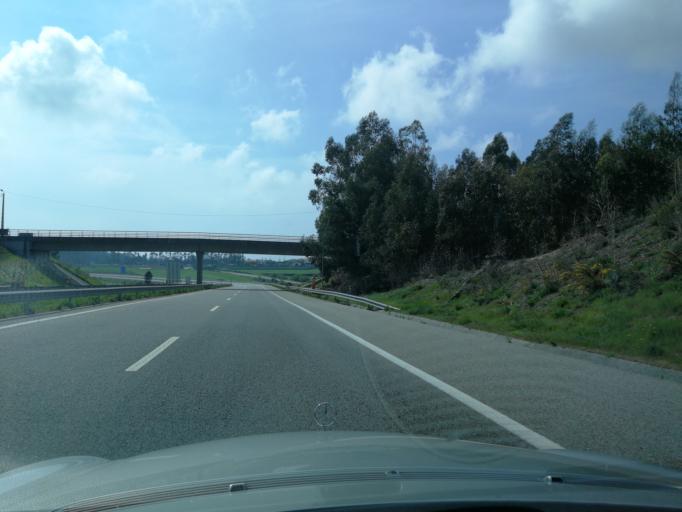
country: PT
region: Porto
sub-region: Vila do Conde
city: Vila do Conde
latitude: 41.3848
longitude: -8.7089
